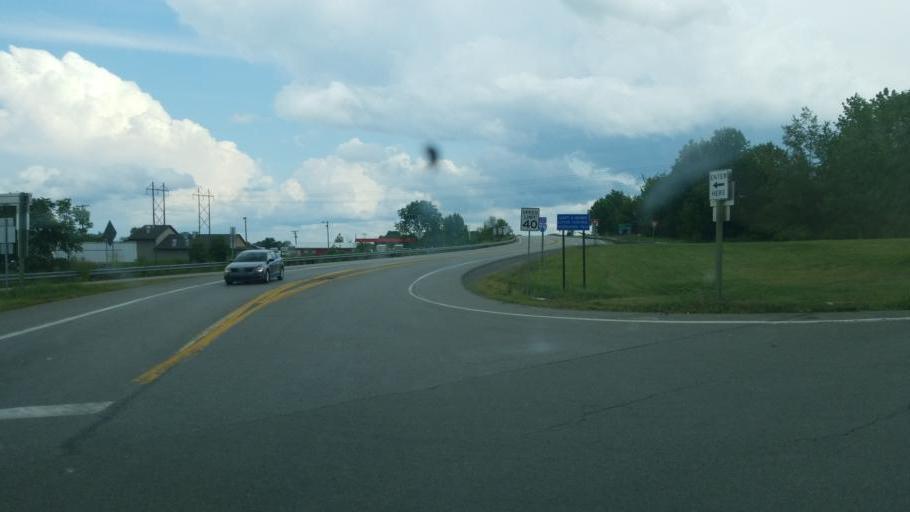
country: US
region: Pennsylvania
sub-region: Crawford County
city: Meadville
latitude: 41.5411
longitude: -80.1874
